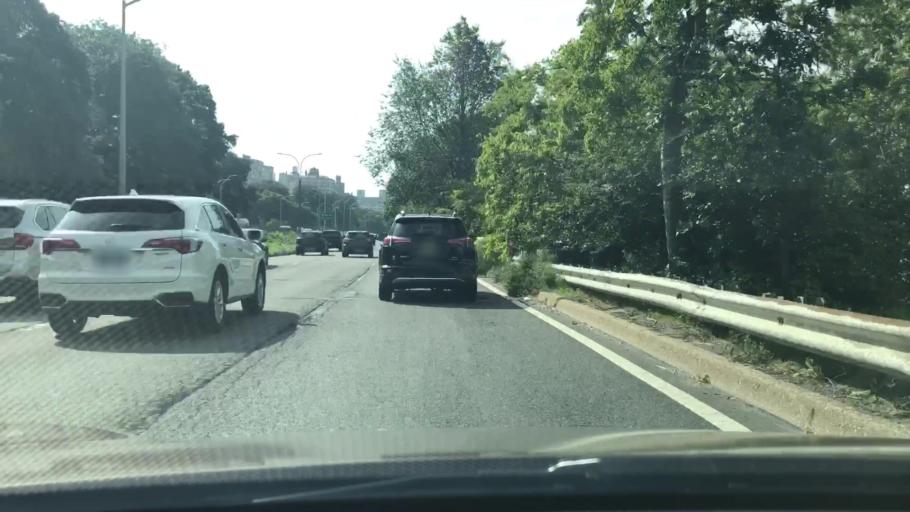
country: US
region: New York
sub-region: New York County
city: Manhattan
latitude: 40.7889
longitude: -73.9826
